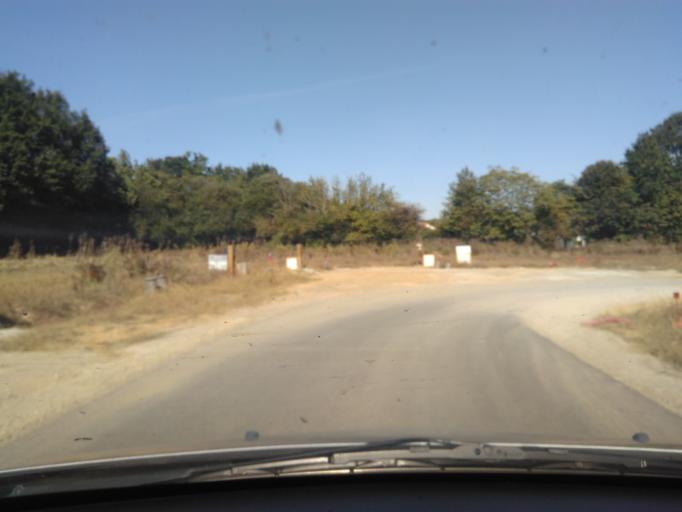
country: FR
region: Pays de la Loire
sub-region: Departement de la Vendee
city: Mouilleron-le-Captif
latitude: 46.7179
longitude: -1.4666
